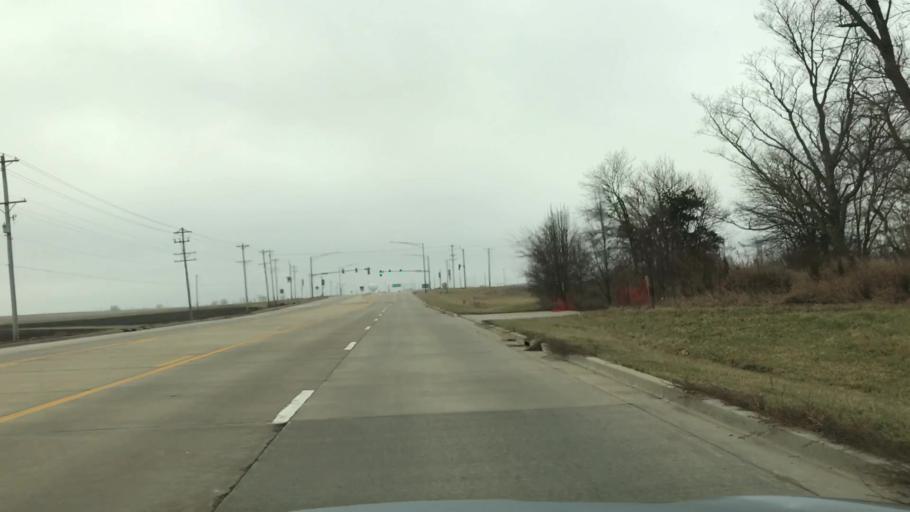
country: US
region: Illinois
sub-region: McLean County
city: Normal
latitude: 40.5494
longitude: -88.9444
